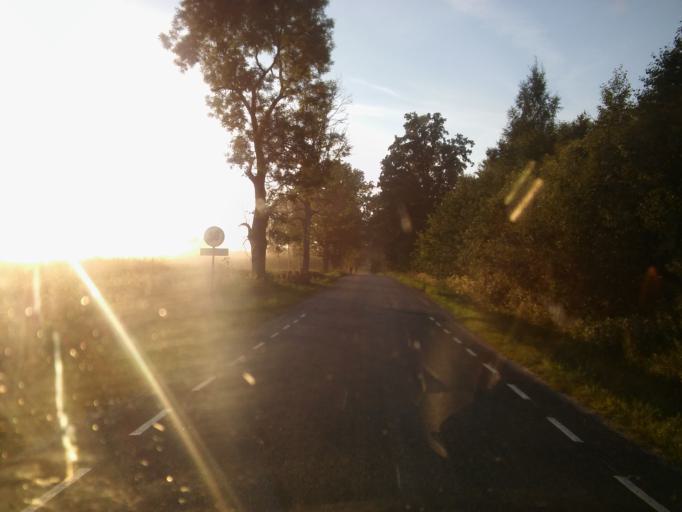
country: EE
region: Viljandimaa
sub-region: Abja vald
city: Abja-Paluoja
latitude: 58.2475
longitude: 25.3248
